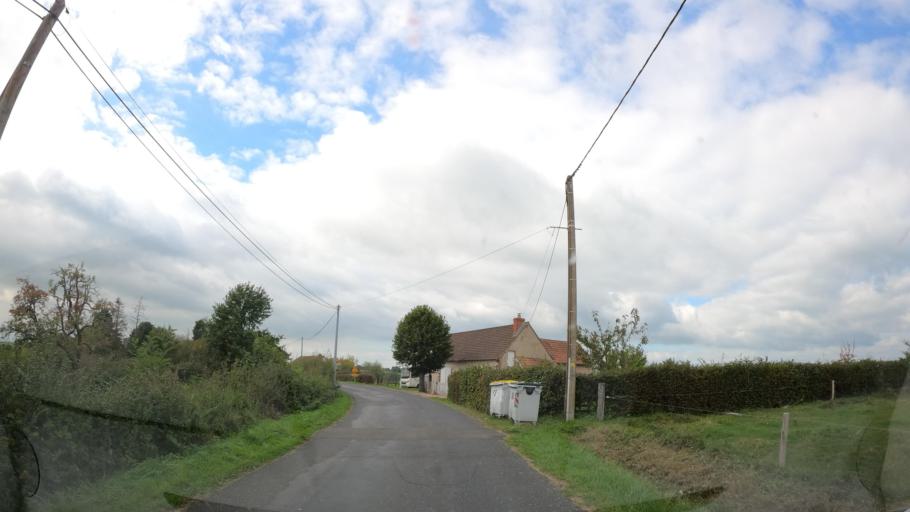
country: FR
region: Auvergne
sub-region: Departement de l'Allier
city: Lapalisse
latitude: 46.3434
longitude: 3.6399
